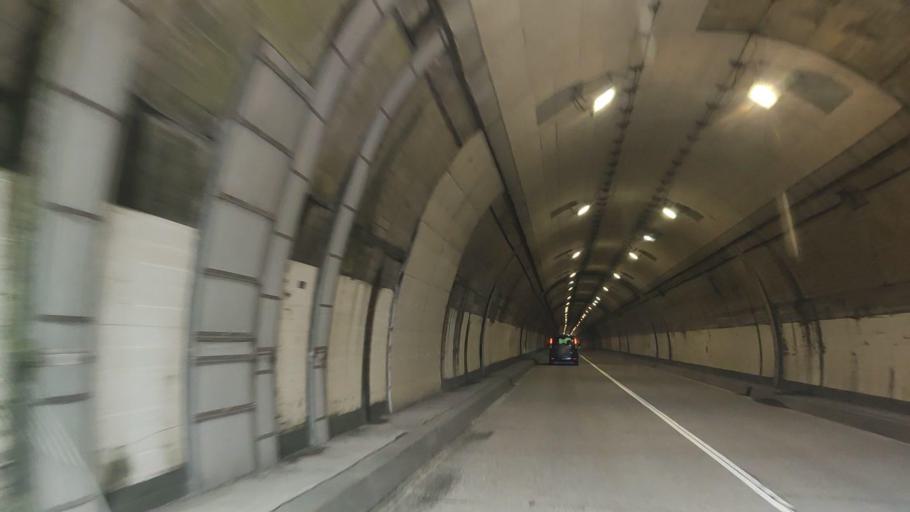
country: JP
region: Hokkaido
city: Niseko Town
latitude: 42.5919
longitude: 140.6750
